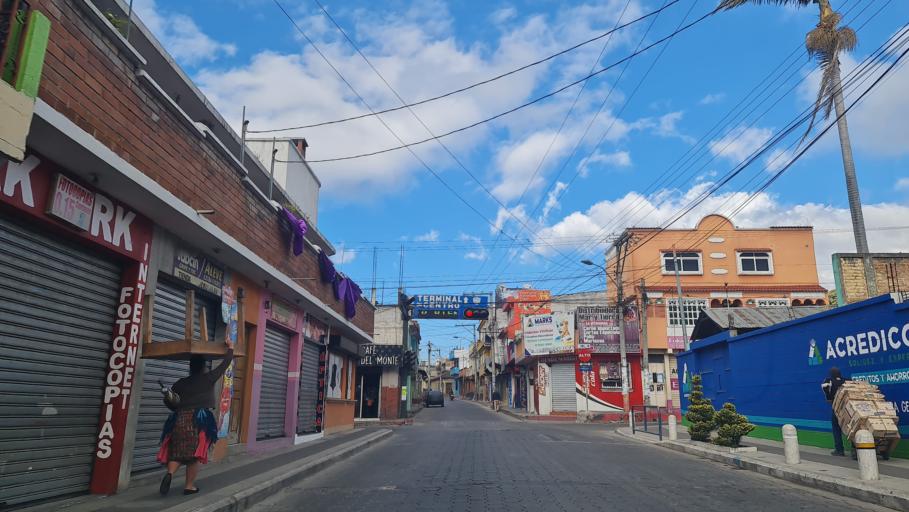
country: GT
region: San Marcos
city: San Pedro Sacatepequez
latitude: 14.9702
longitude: -91.7784
